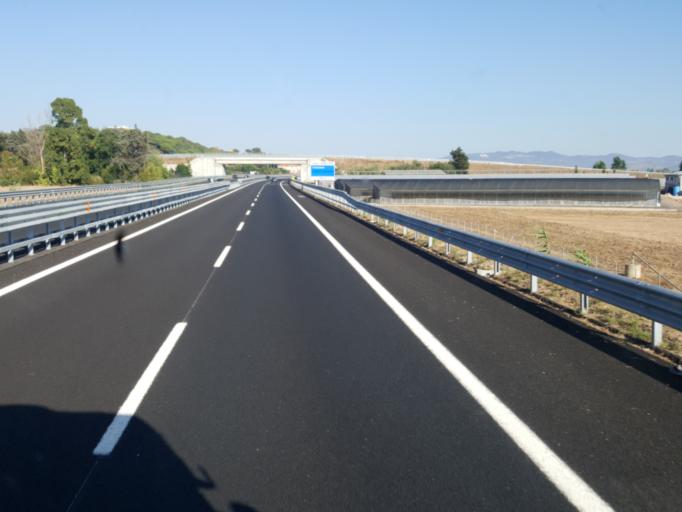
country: IT
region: Latium
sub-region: Provincia di Viterbo
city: Tarquinia
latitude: 42.2412
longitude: 11.7527
